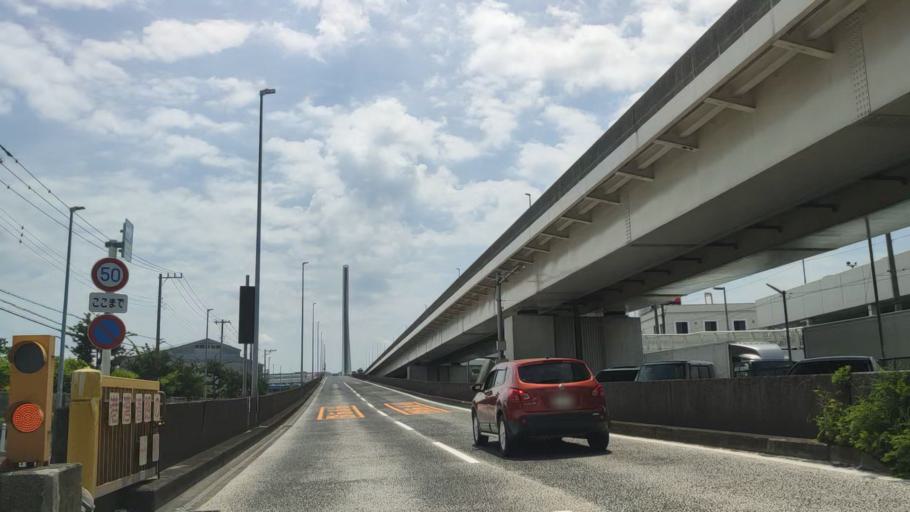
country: JP
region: Kanagawa
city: Yokohama
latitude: 35.4112
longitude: 139.6756
